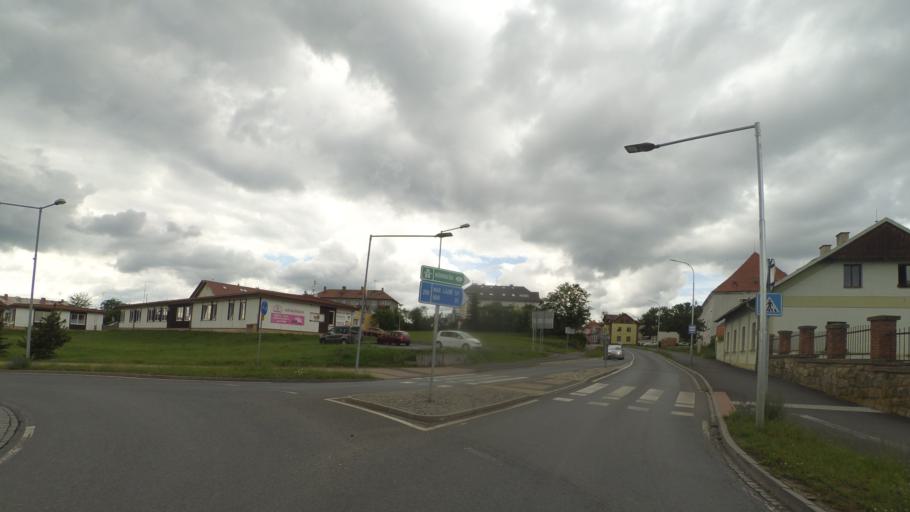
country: CZ
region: Plzensky
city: Horsovsky Tyn
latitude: 49.5288
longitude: 12.9384
